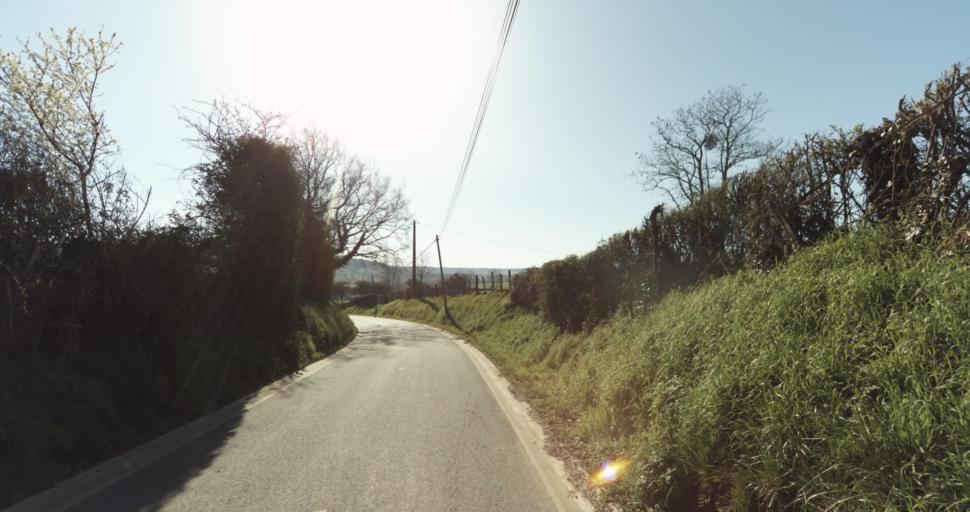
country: FR
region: Lower Normandy
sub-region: Departement du Calvados
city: Saint-Pierre-sur-Dives
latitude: 48.9886
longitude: 0.0237
